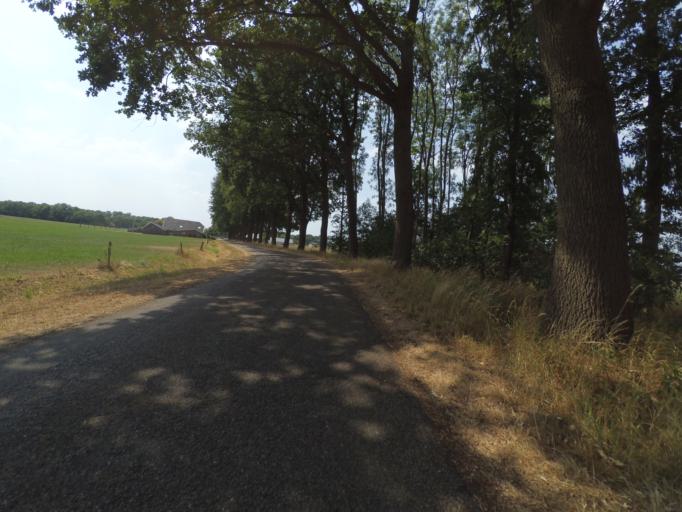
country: DE
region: North Rhine-Westphalia
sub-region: Regierungsbezirk Munster
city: Isselburg
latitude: 51.8705
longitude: 6.4334
